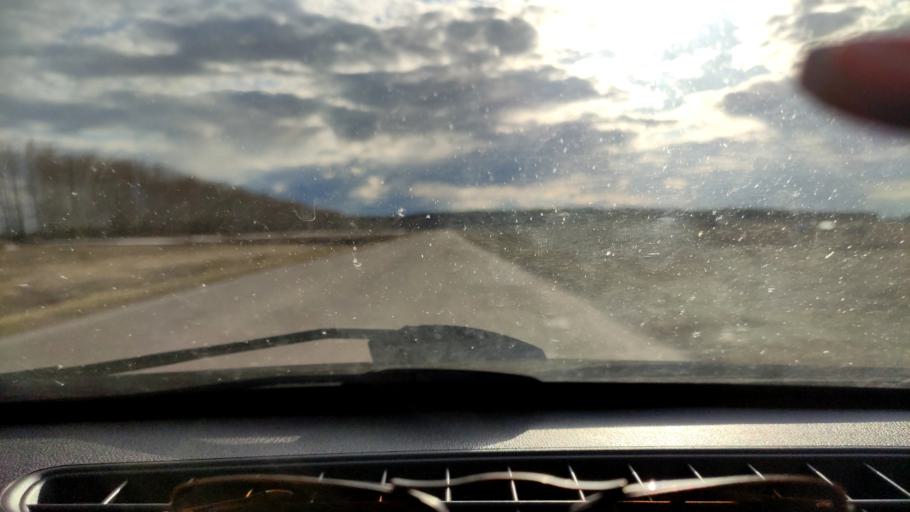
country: RU
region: Bashkortostan
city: Karmaskaly
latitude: 54.3453
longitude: 56.1072
